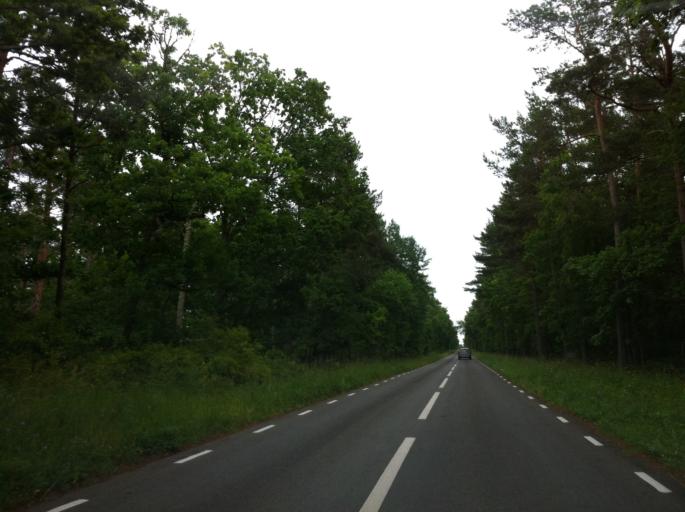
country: SE
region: Kalmar
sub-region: Vasterviks Kommun
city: Vaestervik
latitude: 57.3542
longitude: 17.0566
